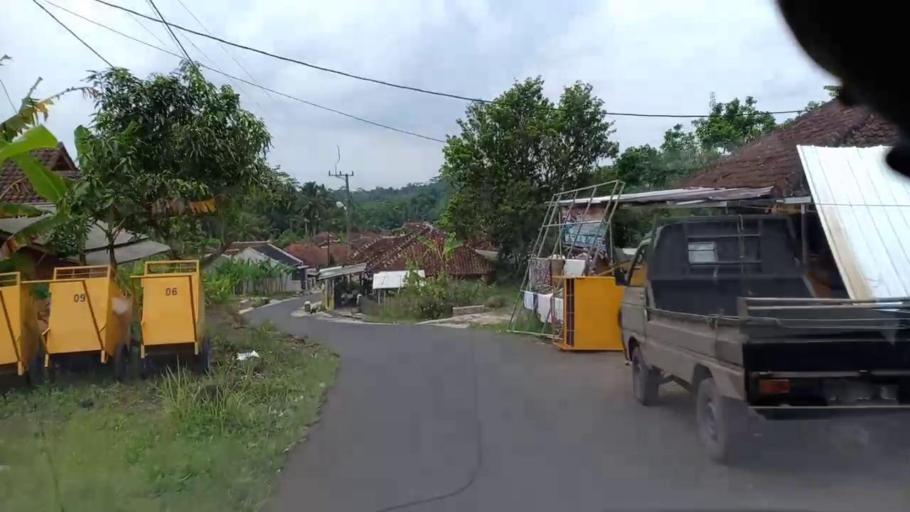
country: ID
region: West Java
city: Gerempay
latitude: -7.3377
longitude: 108.2846
